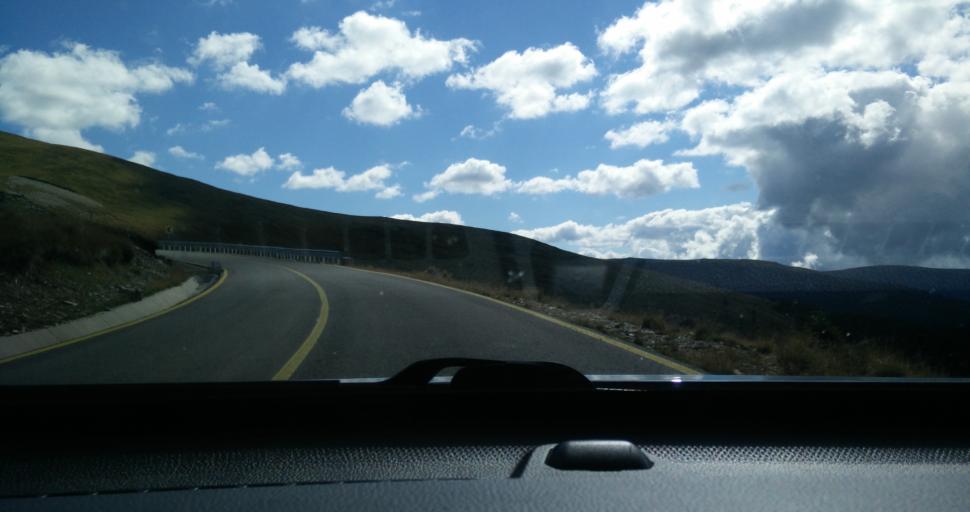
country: RO
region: Gorj
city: Novaci-Straini
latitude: 45.3150
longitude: 23.6817
